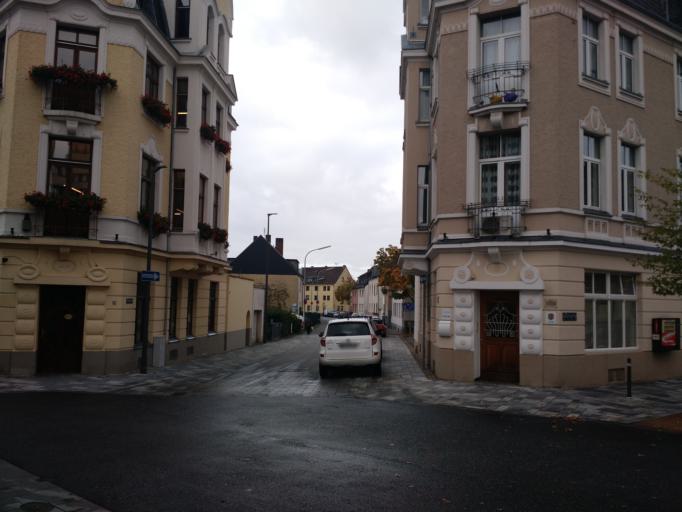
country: DE
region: North Rhine-Westphalia
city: Wesseling
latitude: 50.8245
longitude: 6.9808
